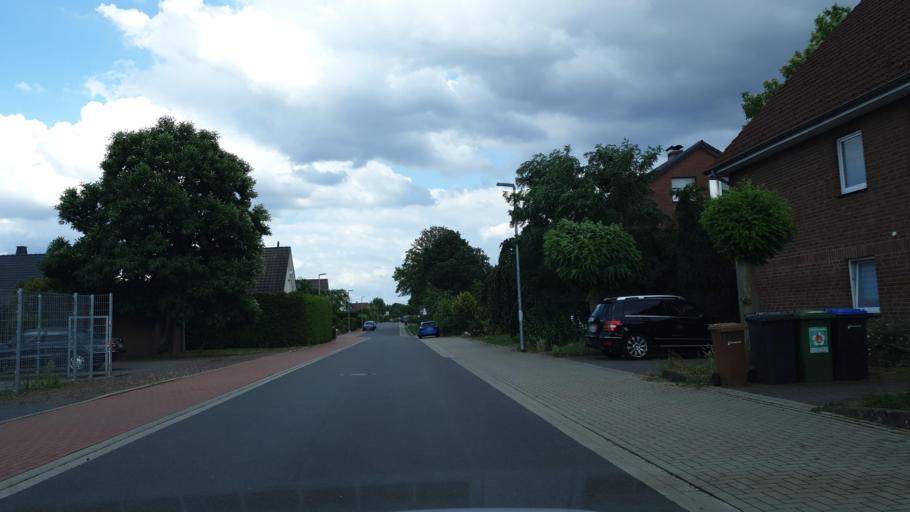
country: DE
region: North Rhine-Westphalia
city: Loehne
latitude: 52.2128
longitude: 8.7263
